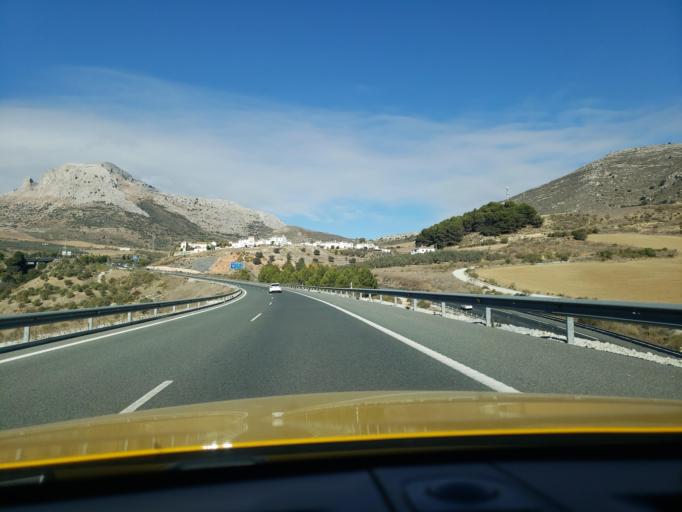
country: ES
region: Andalusia
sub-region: Provincia de Malaga
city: Casabermeja
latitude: 36.9487
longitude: -4.4401
